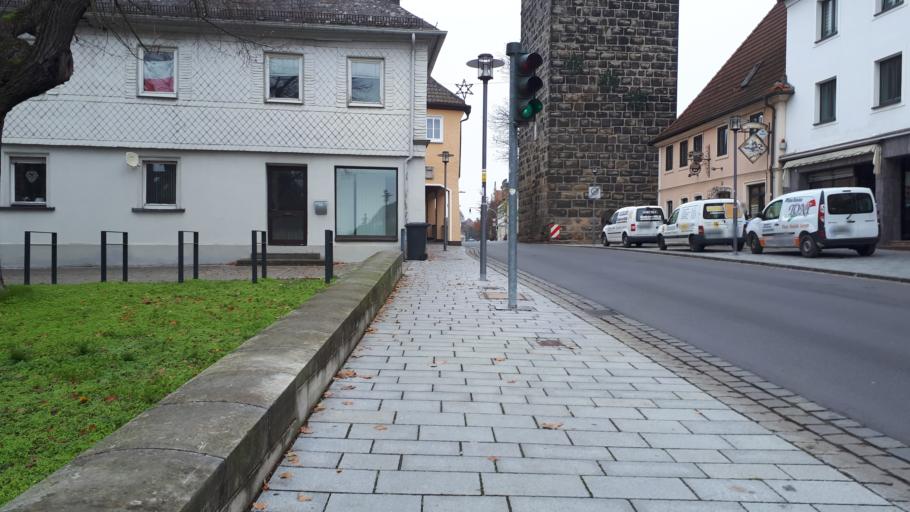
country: DE
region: Bavaria
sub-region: Upper Franconia
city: Lichtenfels
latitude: 50.1467
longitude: 11.0657
